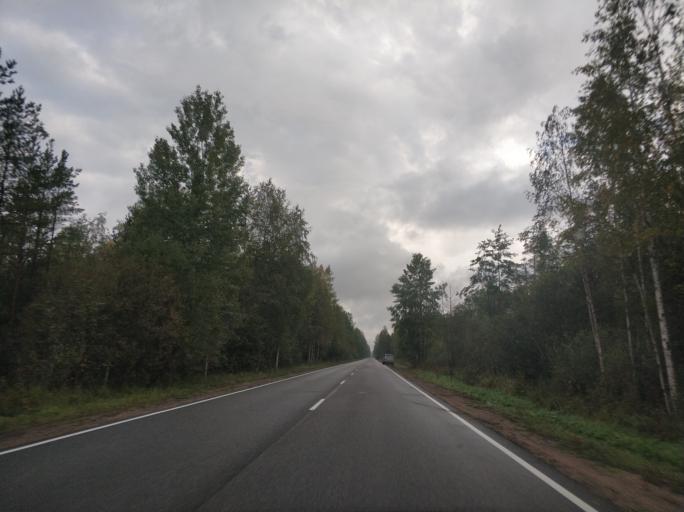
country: RU
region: Leningrad
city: Borisova Griva
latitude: 60.1430
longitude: 30.9482
